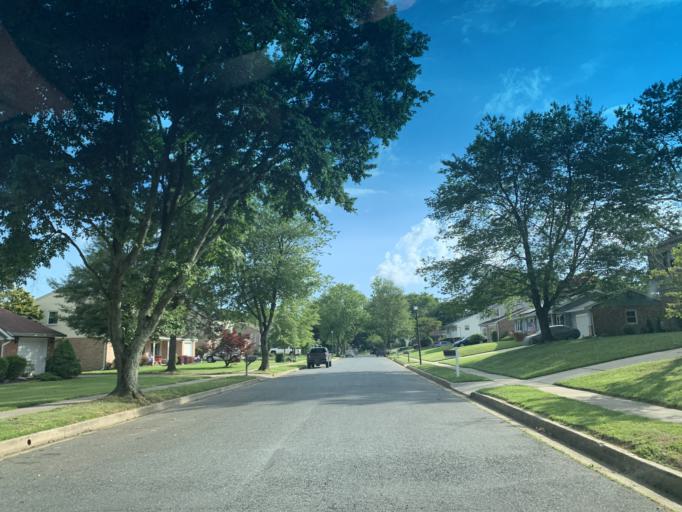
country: US
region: Maryland
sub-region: Harford County
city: South Bel Air
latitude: 39.5317
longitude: -76.3318
